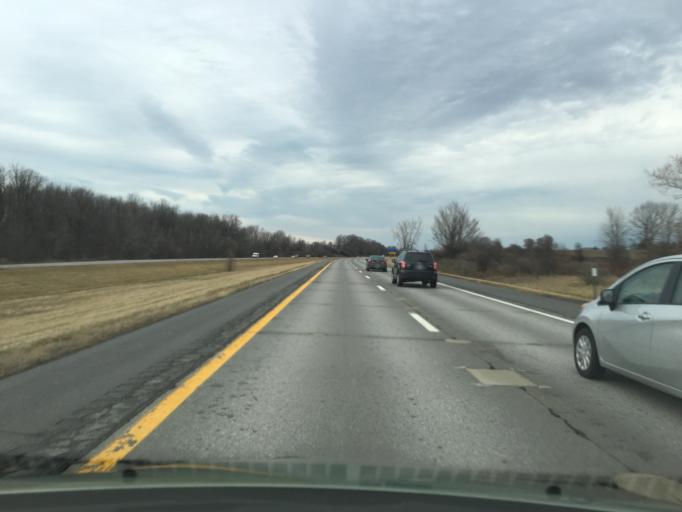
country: US
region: New York
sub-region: Monroe County
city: Scottsville
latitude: 43.0301
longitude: -77.6551
